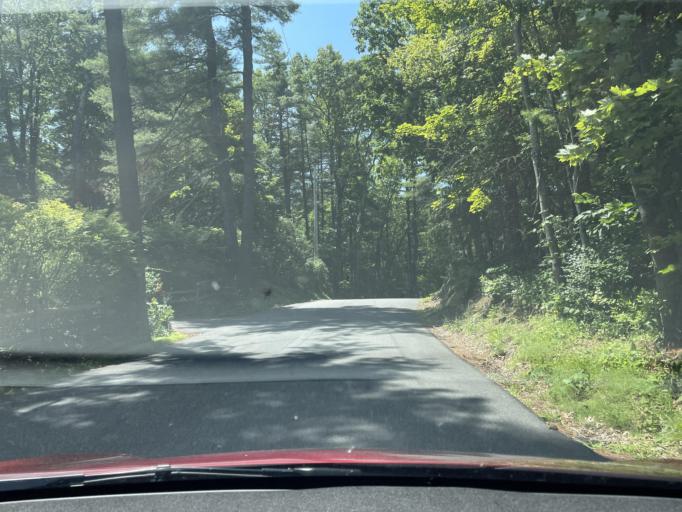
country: US
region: New York
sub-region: Ulster County
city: Lake Katrine
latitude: 41.9989
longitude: -73.9831
